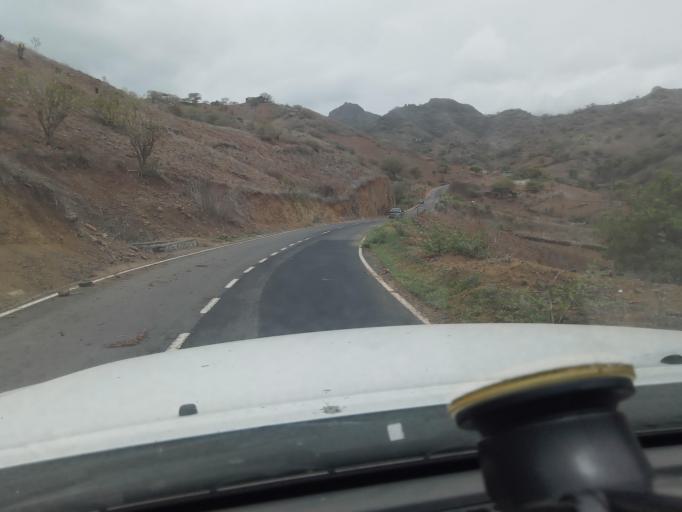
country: CV
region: Sao Miguel
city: Calheta
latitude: 15.1447
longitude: -23.6149
